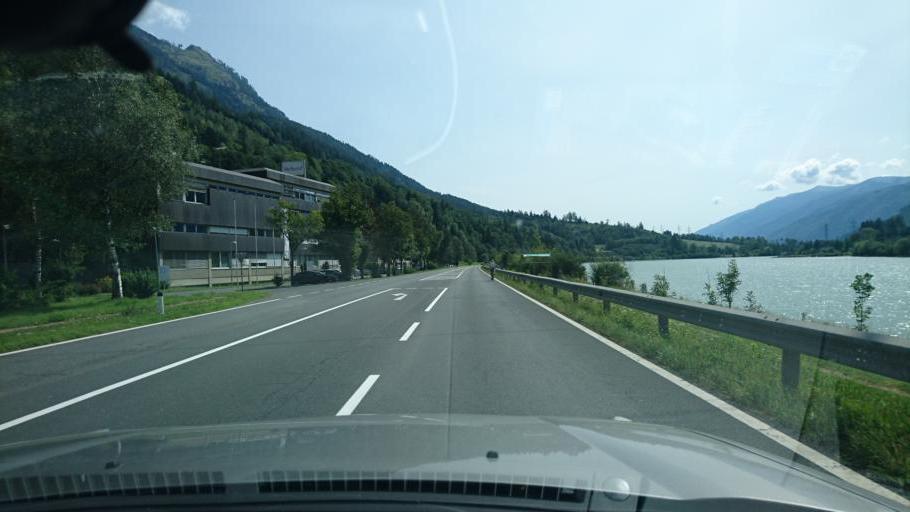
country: AT
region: Carinthia
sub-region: Politischer Bezirk Spittal an der Drau
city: Muhldorf
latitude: 46.8701
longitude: 13.3277
